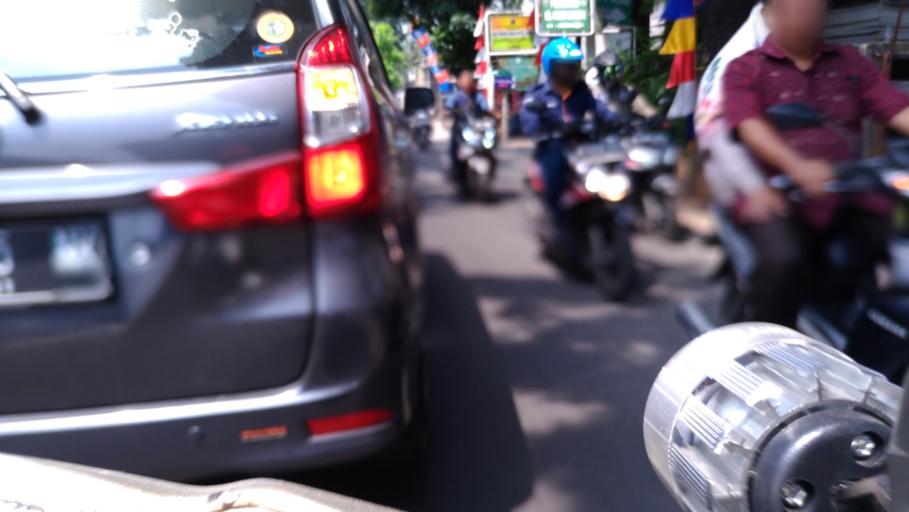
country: ID
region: West Java
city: Cileungsir
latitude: -6.3500
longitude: 106.8957
